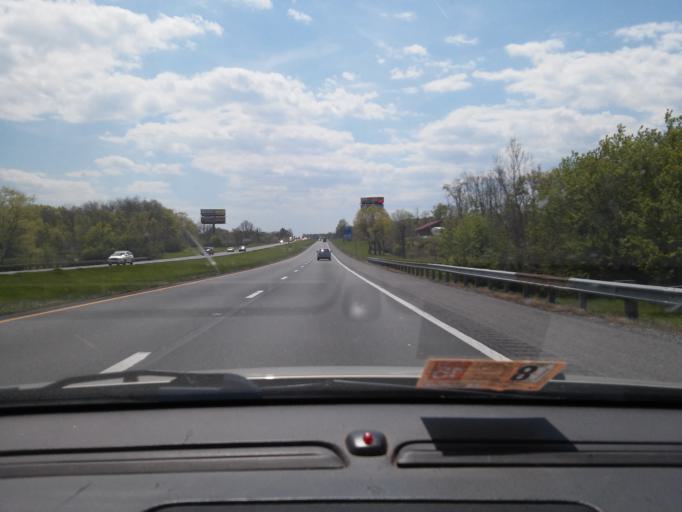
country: US
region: West Virginia
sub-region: Berkeley County
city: Inwood
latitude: 39.3753
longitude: -78.0373
